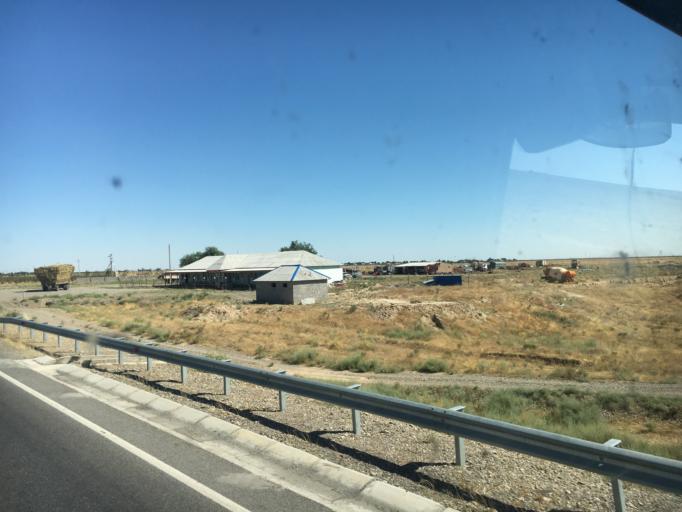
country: KZ
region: Ongtustik Qazaqstan
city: Turkestan
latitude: 43.5107
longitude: 67.8245
